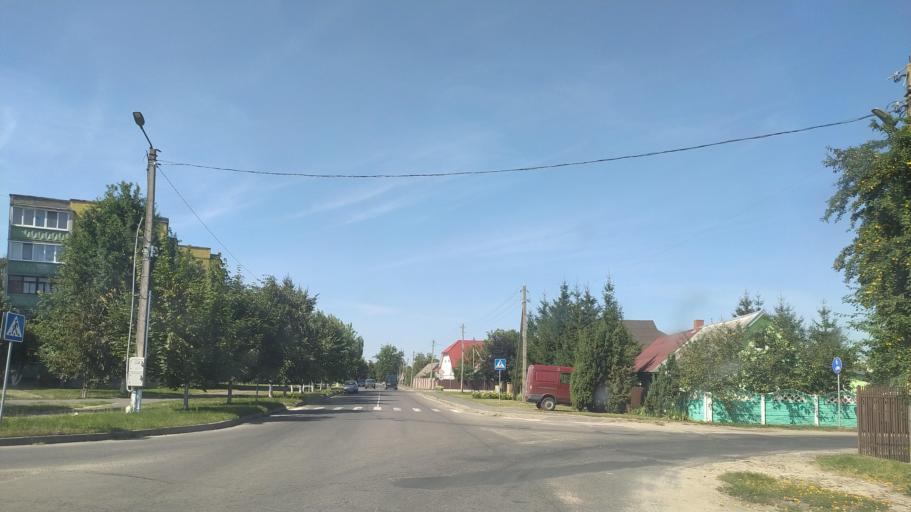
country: BY
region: Brest
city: Byaroza
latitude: 52.5280
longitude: 24.9883
